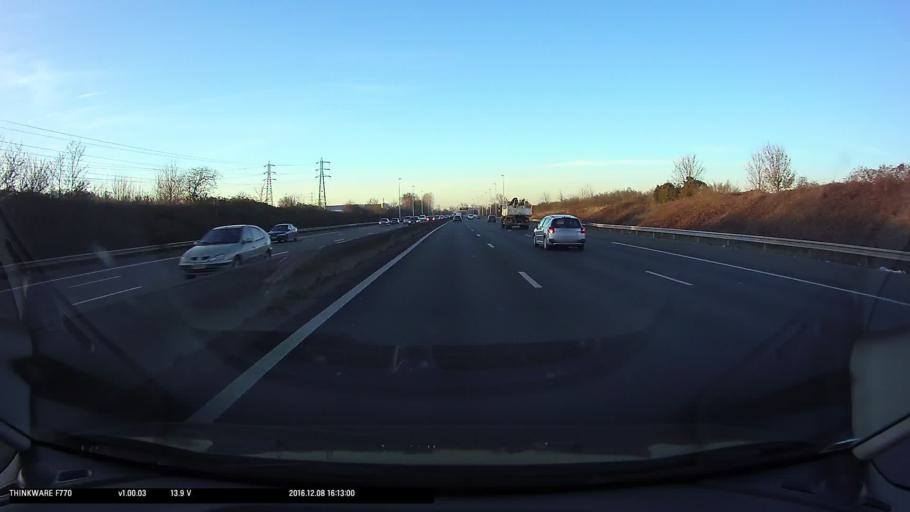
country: FR
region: Ile-de-France
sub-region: Departement du Val-d'Oise
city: Pierrelaye
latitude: 49.0241
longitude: 2.1331
